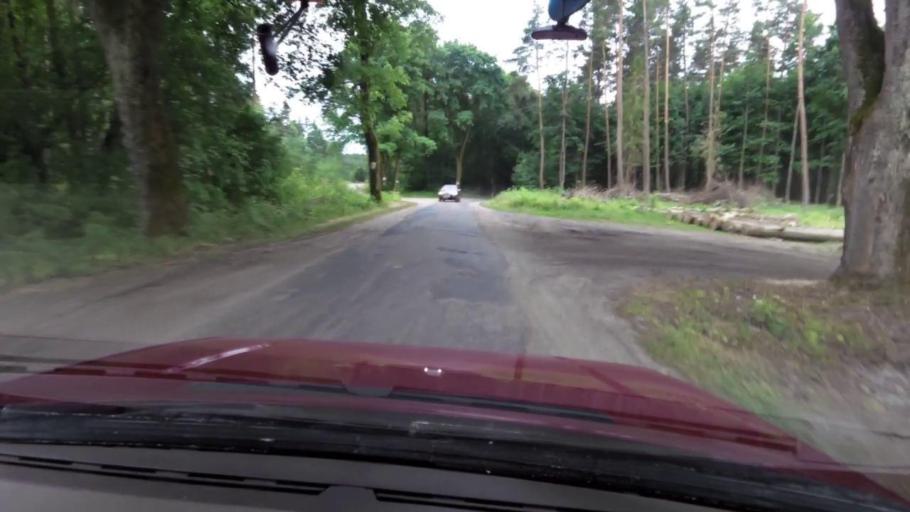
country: PL
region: Pomeranian Voivodeship
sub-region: Powiat slupski
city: Kepice
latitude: 54.1967
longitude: 16.8124
